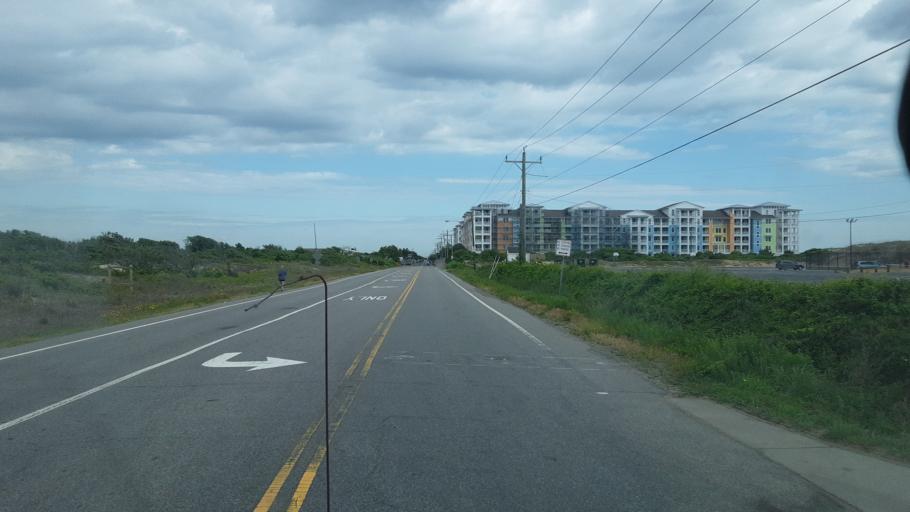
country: US
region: Virginia
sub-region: City of Virginia Beach
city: Virginia Beach
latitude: 36.6934
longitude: -75.9252
